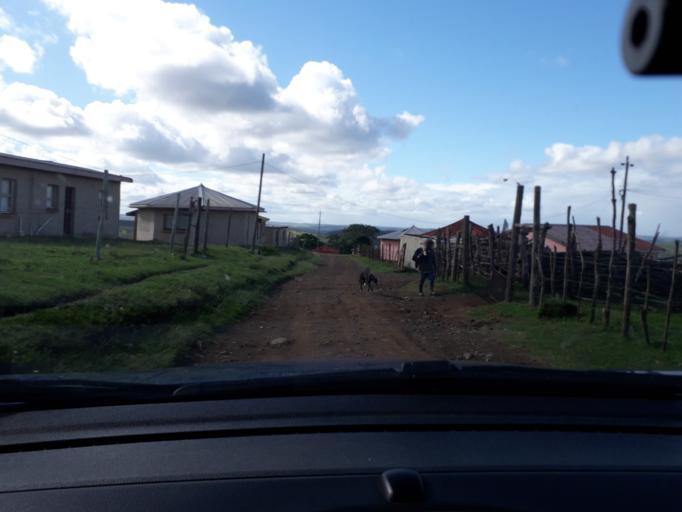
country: ZA
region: Eastern Cape
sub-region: Buffalo City Metropolitan Municipality
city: Bhisho
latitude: -33.1110
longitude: 27.4257
